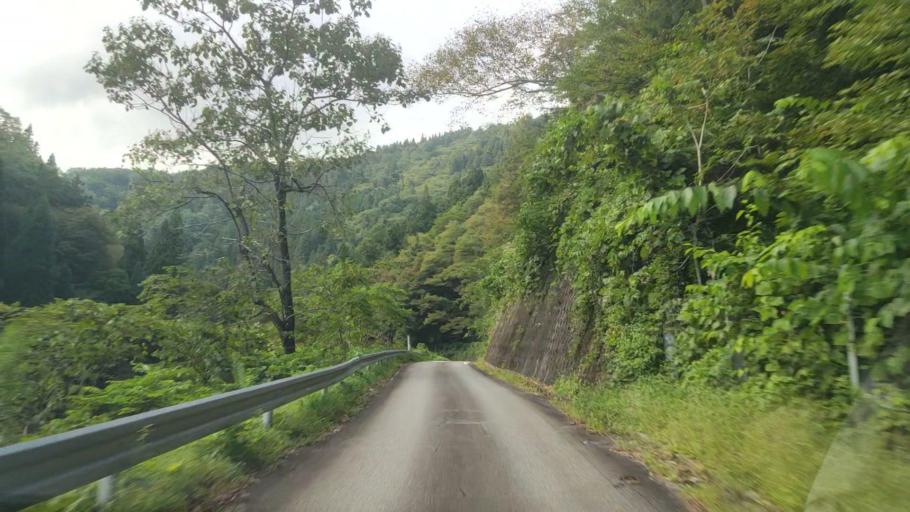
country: JP
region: Gifu
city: Takayama
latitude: 36.3120
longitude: 137.0934
